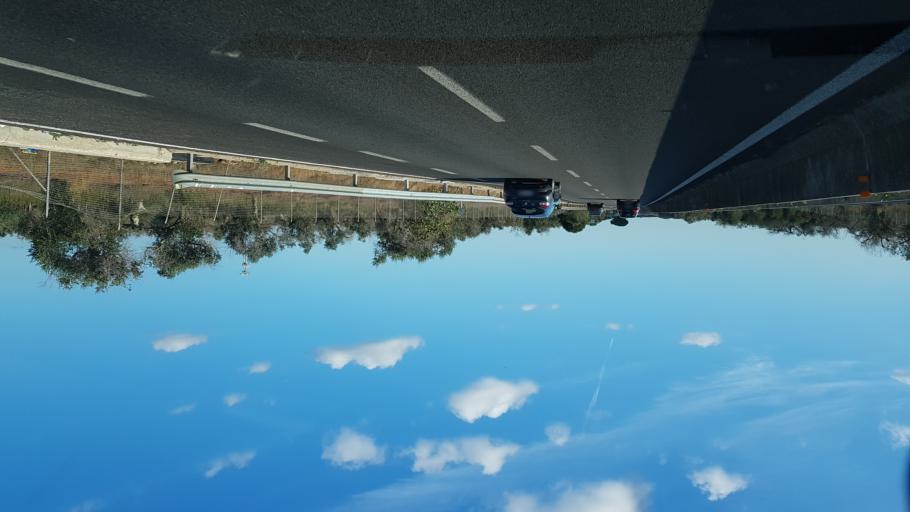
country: IT
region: Apulia
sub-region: Provincia di Lecce
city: Squinzano
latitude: 40.4475
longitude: 18.0716
